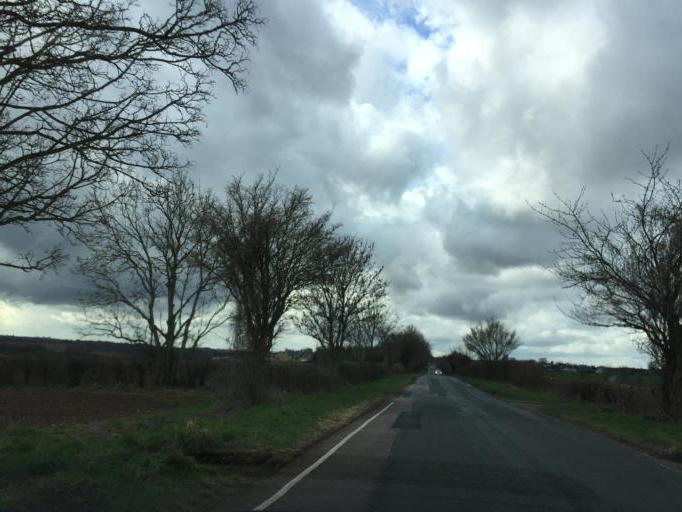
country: GB
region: England
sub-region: Oxfordshire
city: Stonesfield
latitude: 51.8555
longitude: -1.4179
